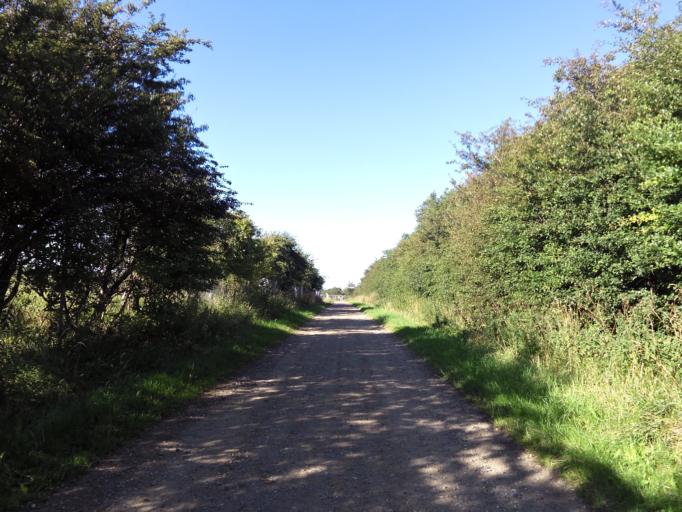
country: DK
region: South Denmark
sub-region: Tonder Kommune
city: Sherrebek
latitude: 55.1545
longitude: 8.7436
